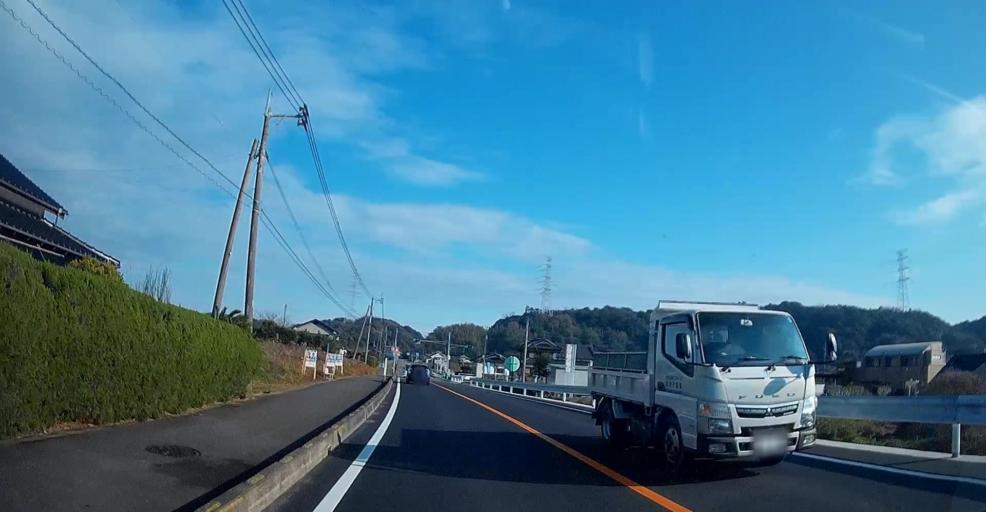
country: JP
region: Kumamoto
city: Yatsushiro
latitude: 32.5193
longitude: 130.4482
